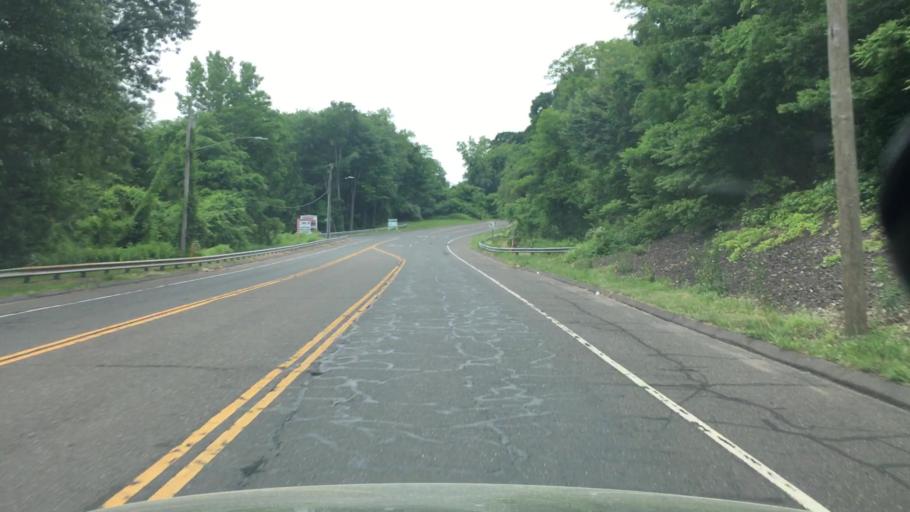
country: US
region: Connecticut
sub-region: Hartford County
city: Windsor Locks
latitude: 41.9001
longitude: -72.6339
